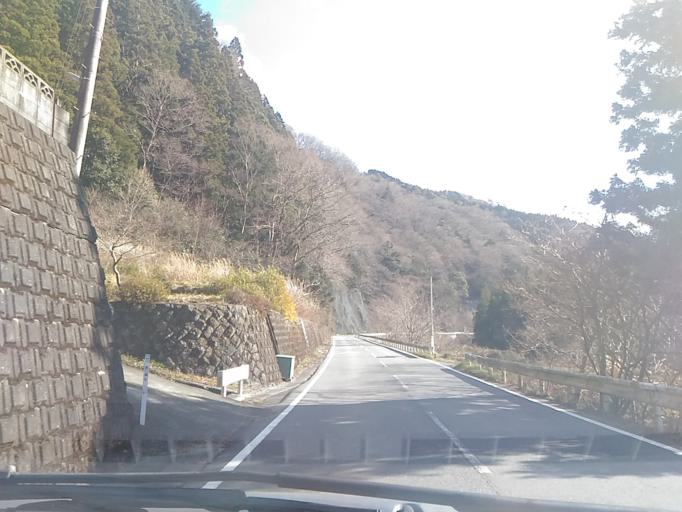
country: JP
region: Fukushima
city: Iwaki
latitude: 37.0194
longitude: 140.6669
